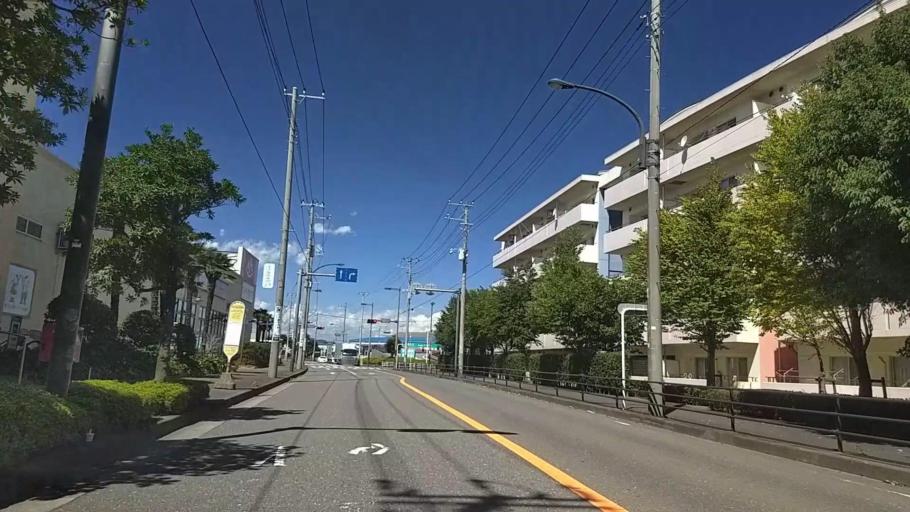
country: JP
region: Kanagawa
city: Zama
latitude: 35.5332
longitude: 139.3518
